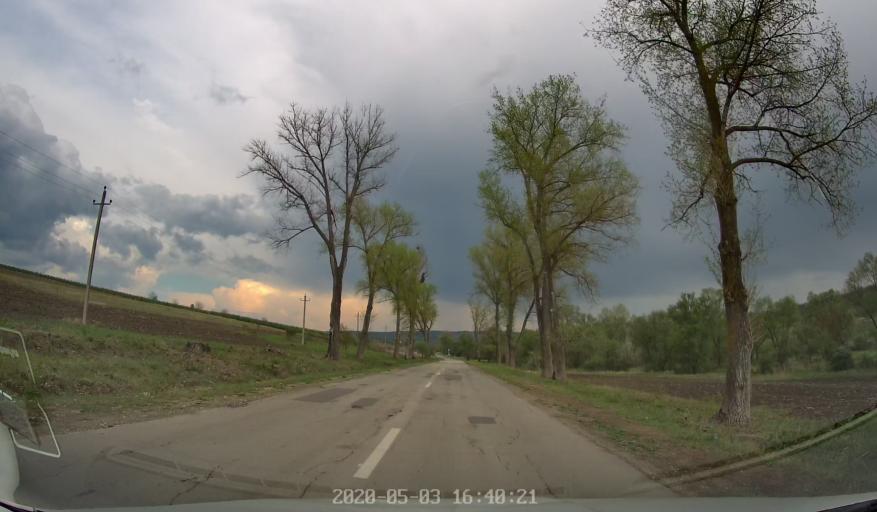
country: MD
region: Stinga Nistrului
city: Bucovat
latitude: 47.1755
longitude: 28.3904
